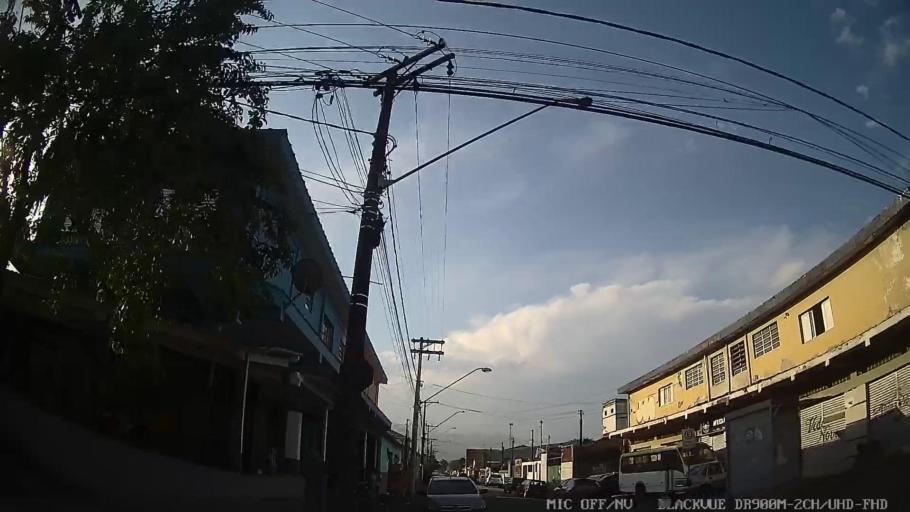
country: BR
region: Sao Paulo
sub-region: Cubatao
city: Cubatao
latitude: -23.9012
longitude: -46.4236
